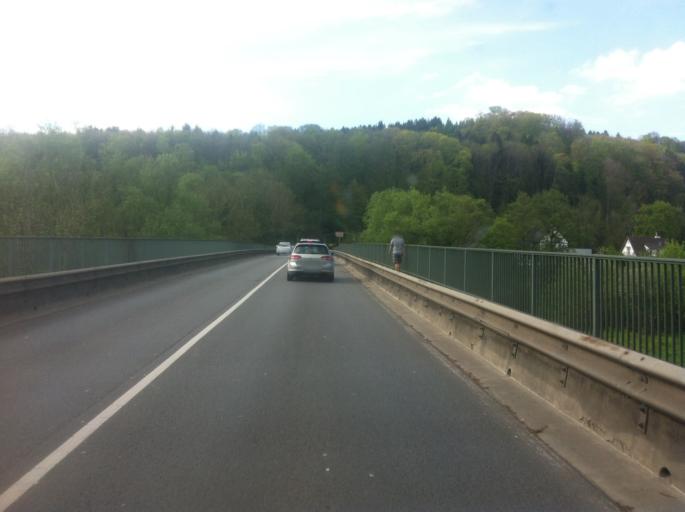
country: DE
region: North Rhine-Westphalia
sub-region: Regierungsbezirk Koln
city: Hennef
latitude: 50.7798
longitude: 7.3053
